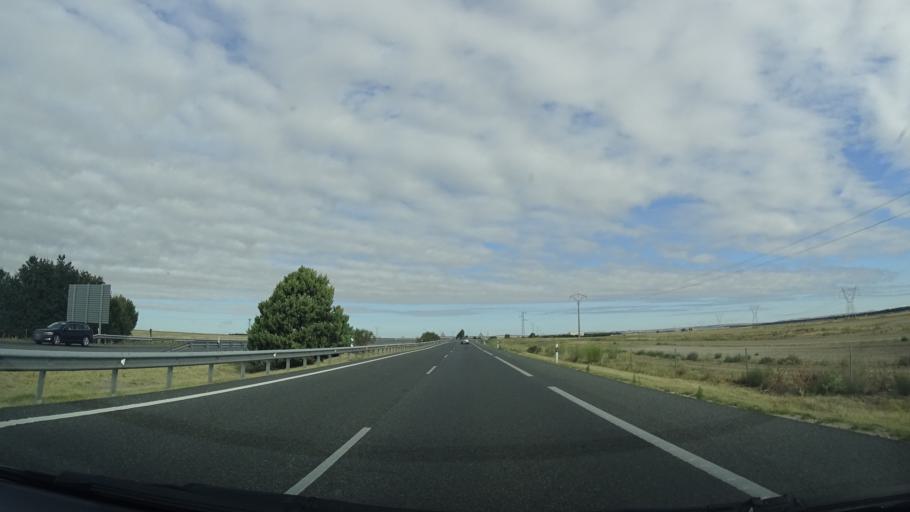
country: ES
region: Castille and Leon
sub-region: Provincia de Valladolid
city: San Vicente del Palacio
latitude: 41.2414
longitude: -4.8632
